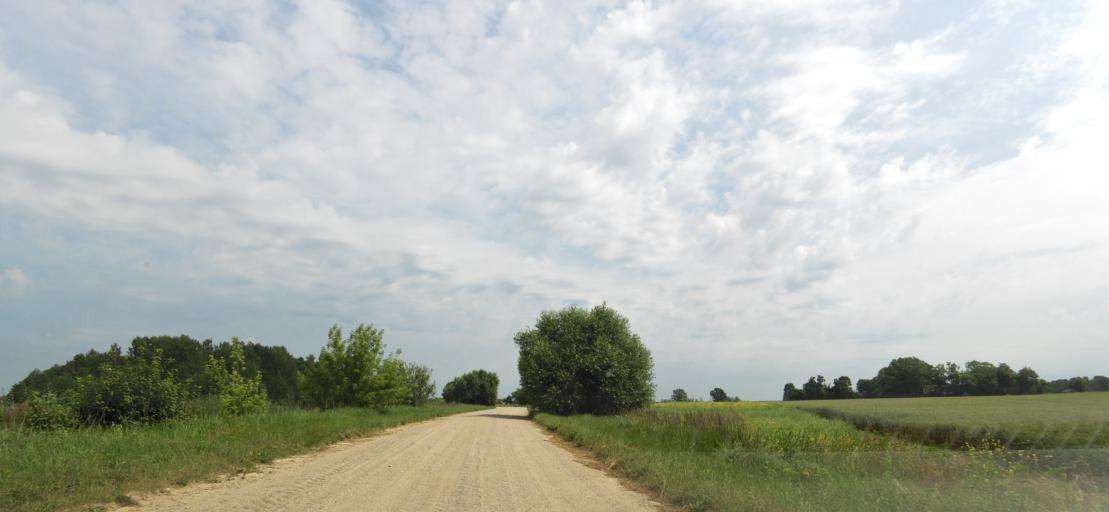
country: LT
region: Panevezys
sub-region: Birzai
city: Birzai
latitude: 56.3215
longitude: 24.6949
